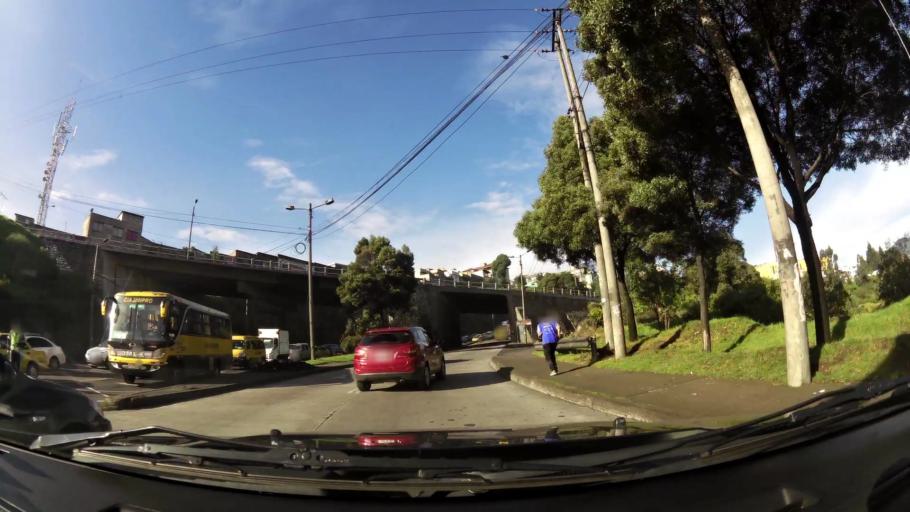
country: EC
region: Pichincha
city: Quito
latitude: -0.2334
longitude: -78.5089
